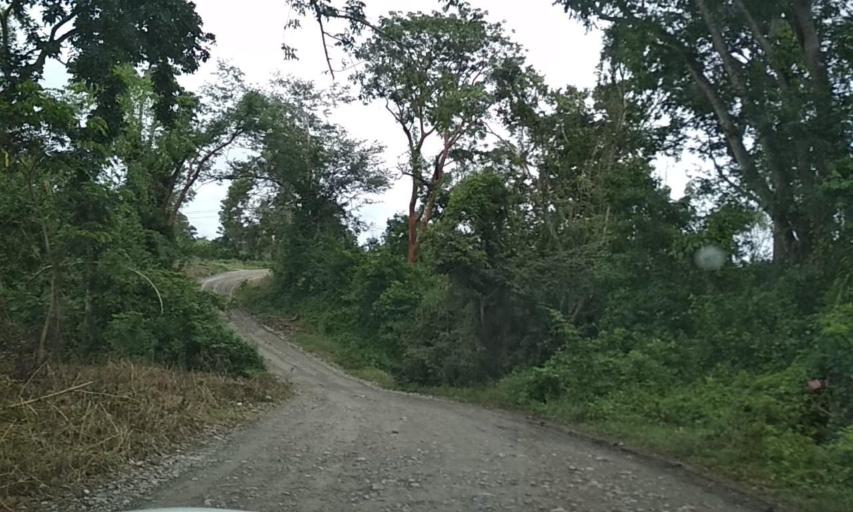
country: MX
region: Puebla
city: Espinal
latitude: 20.3071
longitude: -97.4152
